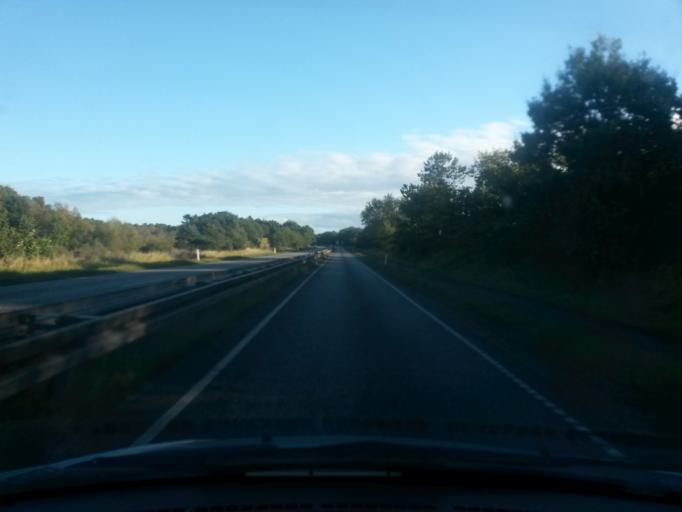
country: DK
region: Central Jutland
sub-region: Viborg Kommune
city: Viborg
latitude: 56.4220
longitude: 9.3862
